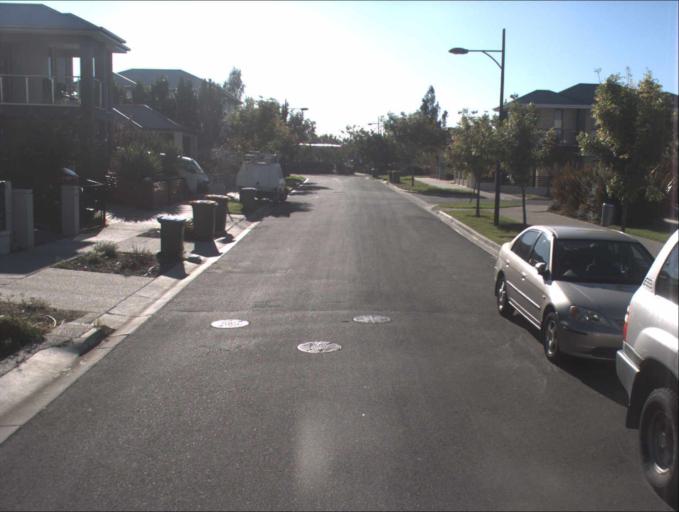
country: AU
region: South Australia
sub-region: Port Adelaide Enfield
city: Klemzig
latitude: -34.8602
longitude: 138.6290
